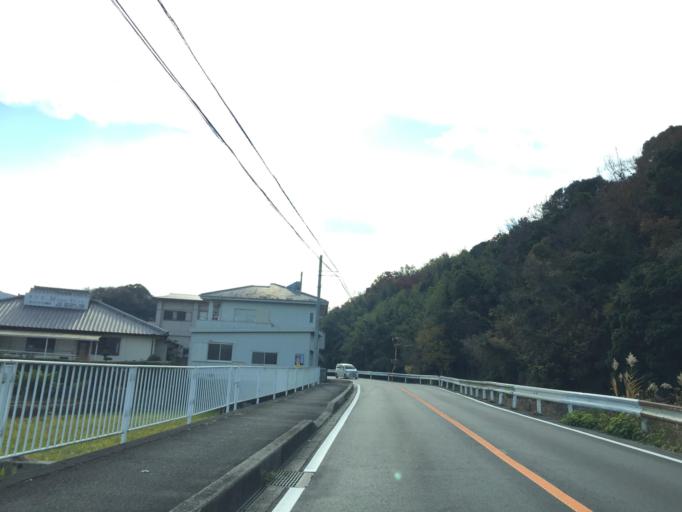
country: JP
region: Wakayama
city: Kainan
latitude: 34.1686
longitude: 135.2506
